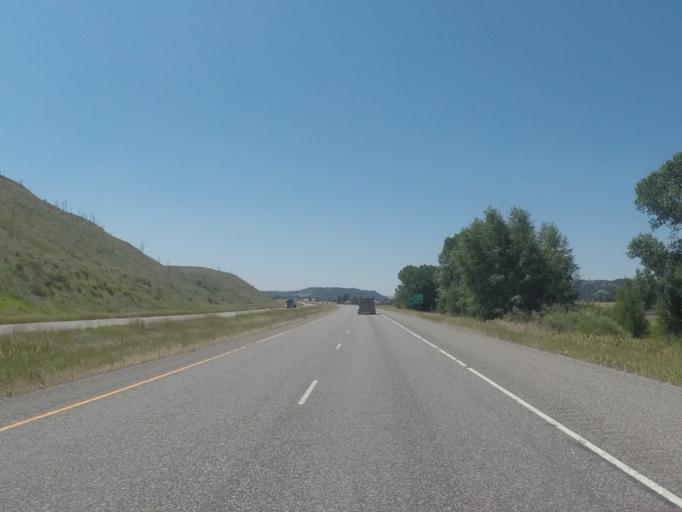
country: US
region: Montana
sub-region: Stillwater County
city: Absarokee
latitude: 45.7083
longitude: -109.5158
